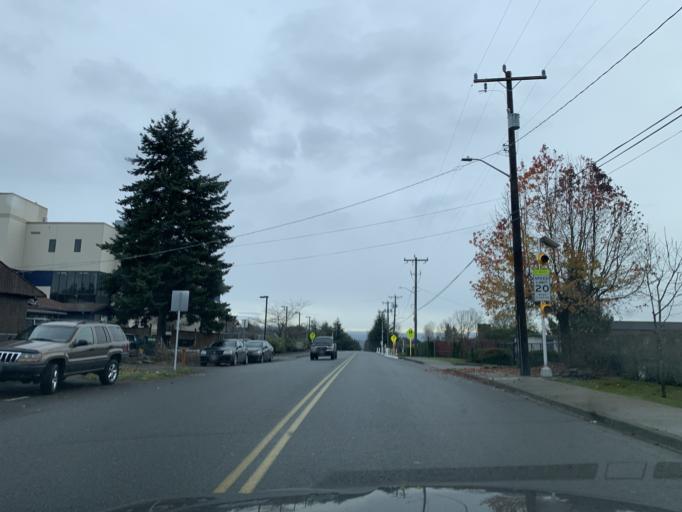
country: US
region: Washington
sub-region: King County
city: Riverton
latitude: 47.4706
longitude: -122.2890
